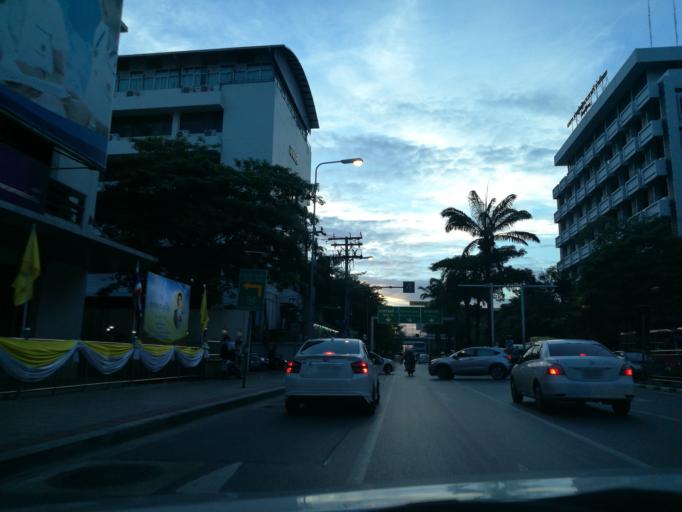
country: TH
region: Bangkok
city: Ratchathewi
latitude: 13.7670
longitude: 100.5341
